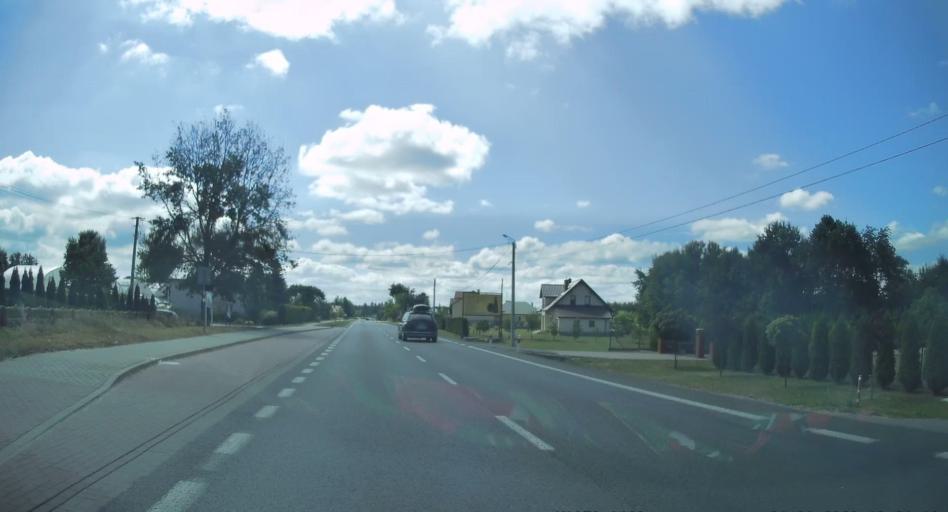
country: PL
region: Subcarpathian Voivodeship
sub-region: Powiat debicki
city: Brzeznica
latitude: 50.1138
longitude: 21.4898
